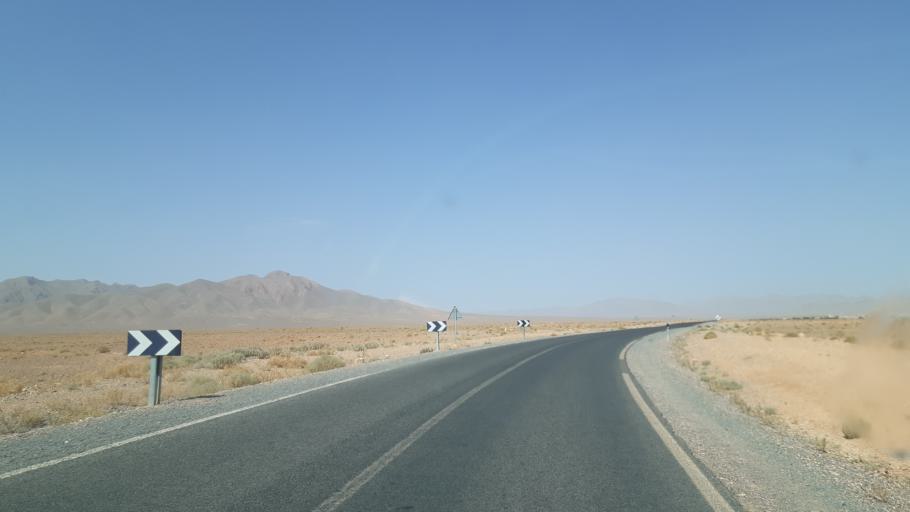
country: MA
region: Meknes-Tafilalet
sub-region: Errachidia
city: Amouguer
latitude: 32.2308
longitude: -4.6499
